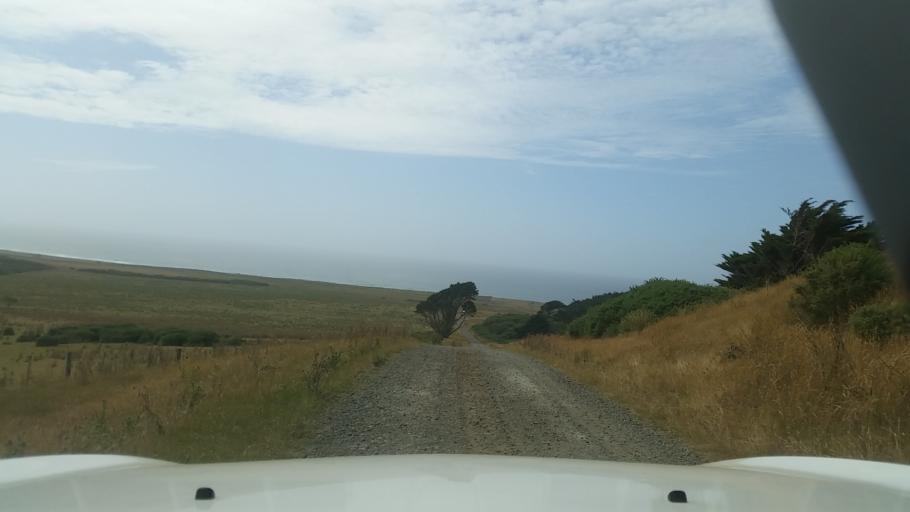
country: NZ
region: Chatham Islands
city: Waitangi
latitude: -43.7157
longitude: -176.5869
